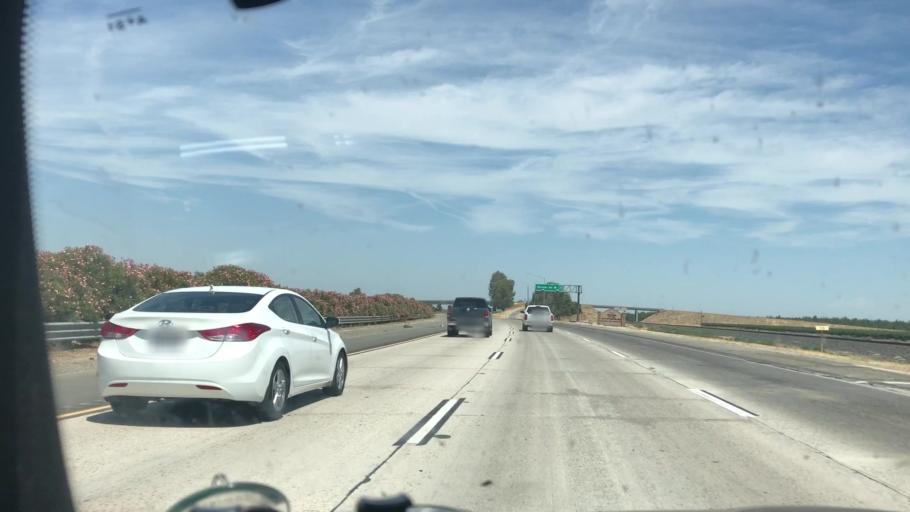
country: US
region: California
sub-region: Kern County
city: McFarland
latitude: 35.6407
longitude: -119.2183
